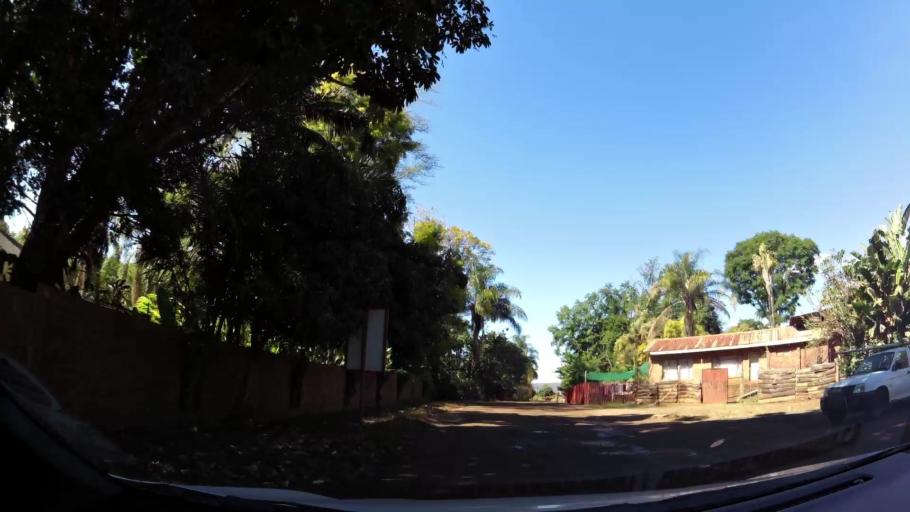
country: ZA
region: Limpopo
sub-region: Mopani District Municipality
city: Tzaneen
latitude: -23.8193
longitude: 30.1557
